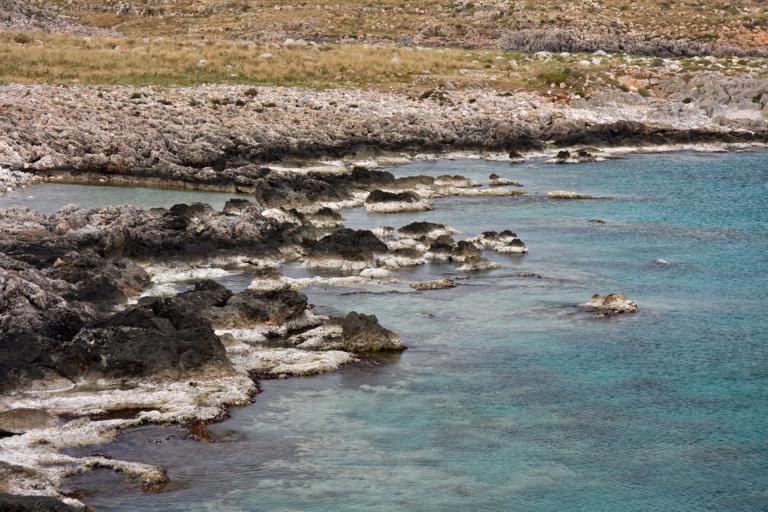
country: GR
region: Peloponnese
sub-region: Nomos Lakonias
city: Gytheio
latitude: 36.3991
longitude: 22.4845
